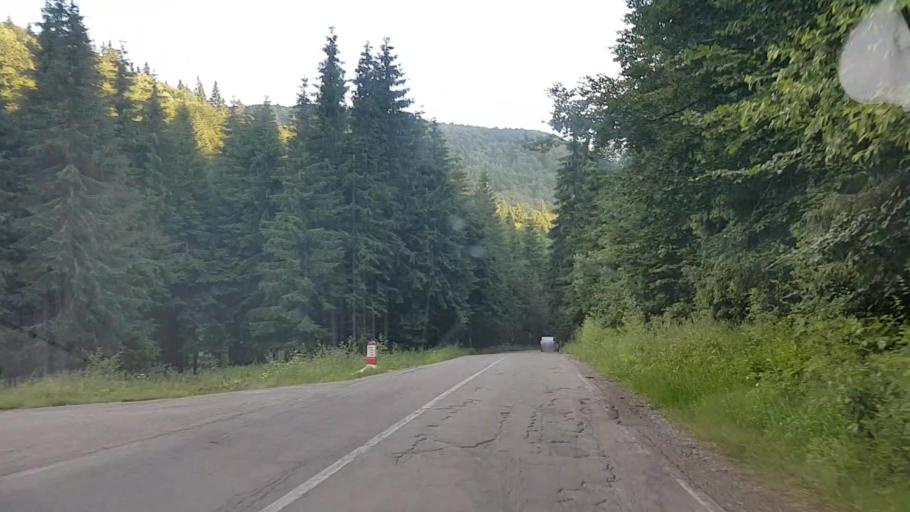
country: RO
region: Harghita
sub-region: Comuna Varsag
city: Varsag
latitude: 46.6334
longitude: 25.2654
